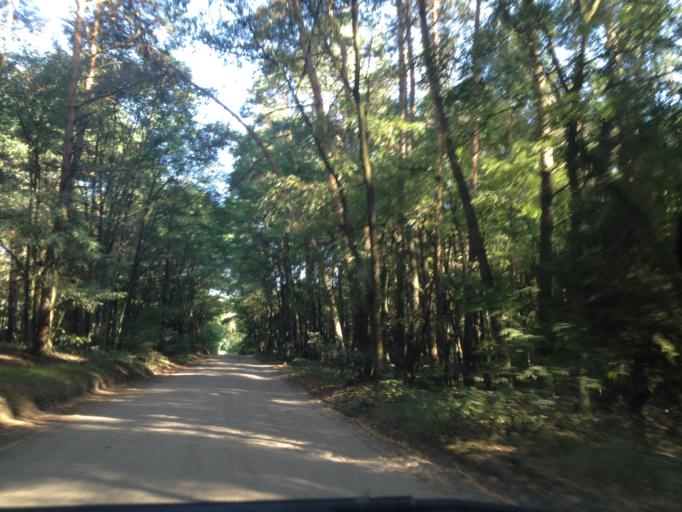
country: PL
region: Greater Poland Voivodeship
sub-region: Powiat sredzki
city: Zaniemysl
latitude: 52.1093
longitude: 17.1232
